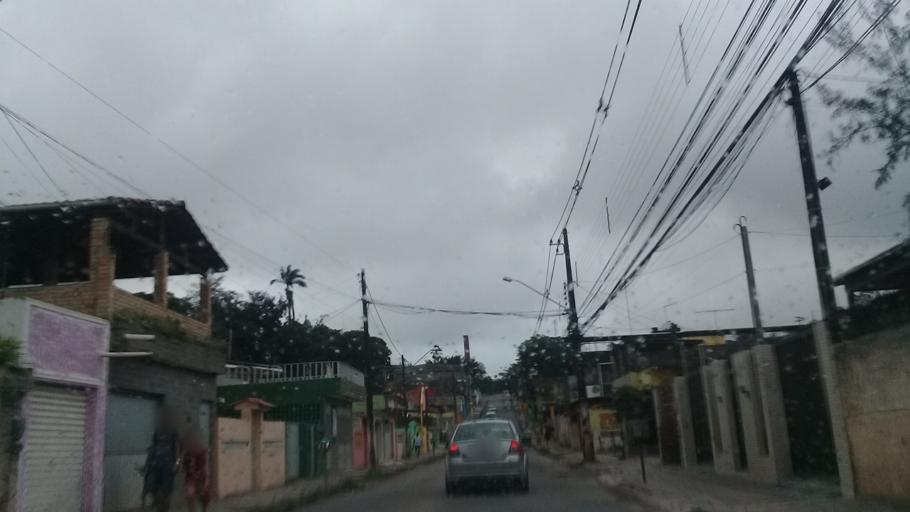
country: BR
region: Pernambuco
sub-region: Moreno
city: Moreno
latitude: -8.1177
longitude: -35.0968
